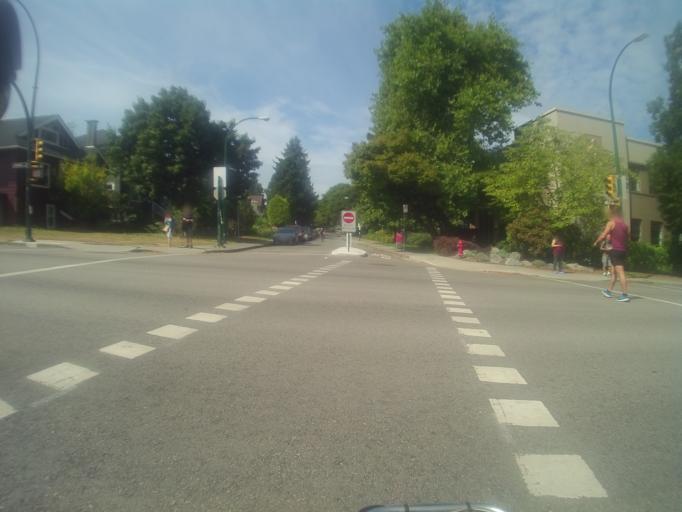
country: CA
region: British Columbia
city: West End
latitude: 49.2627
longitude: -123.1457
